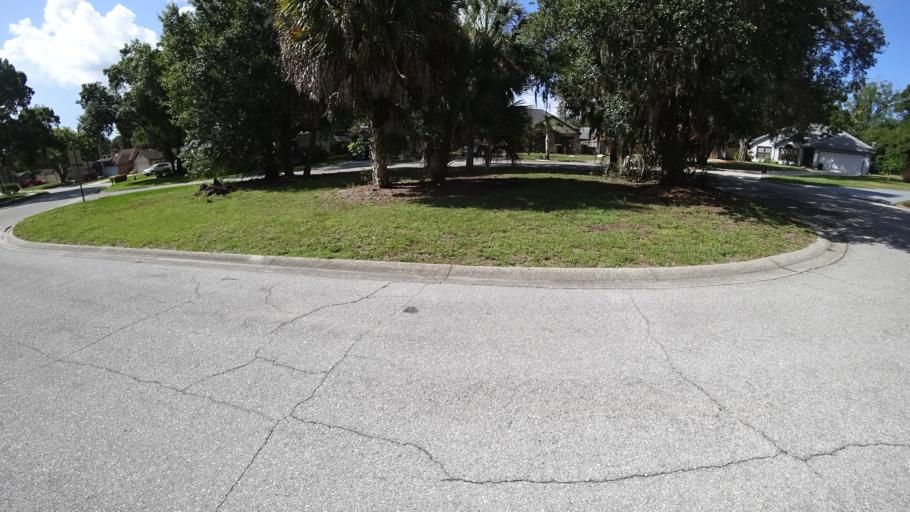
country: US
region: Florida
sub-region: Sarasota County
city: Desoto Lakes
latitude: 27.3955
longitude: -82.4999
